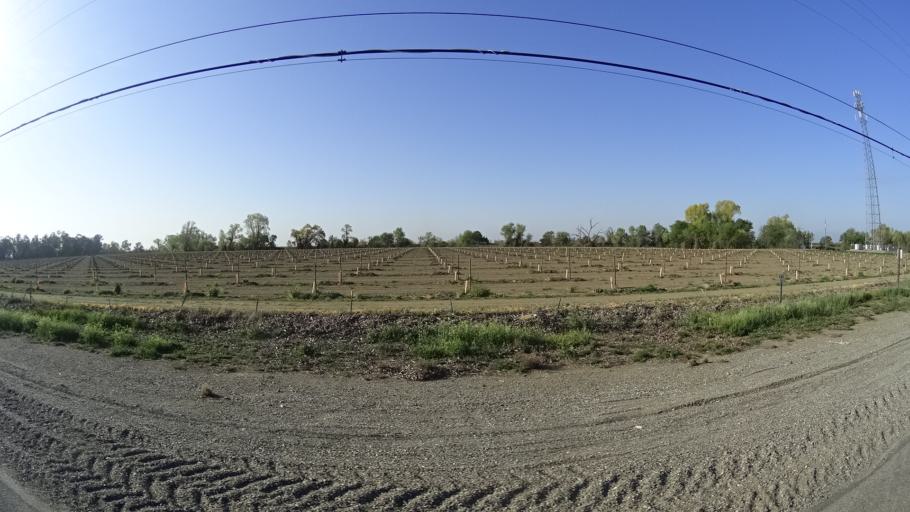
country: US
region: California
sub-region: Glenn County
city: Willows
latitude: 39.5247
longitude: -122.1680
